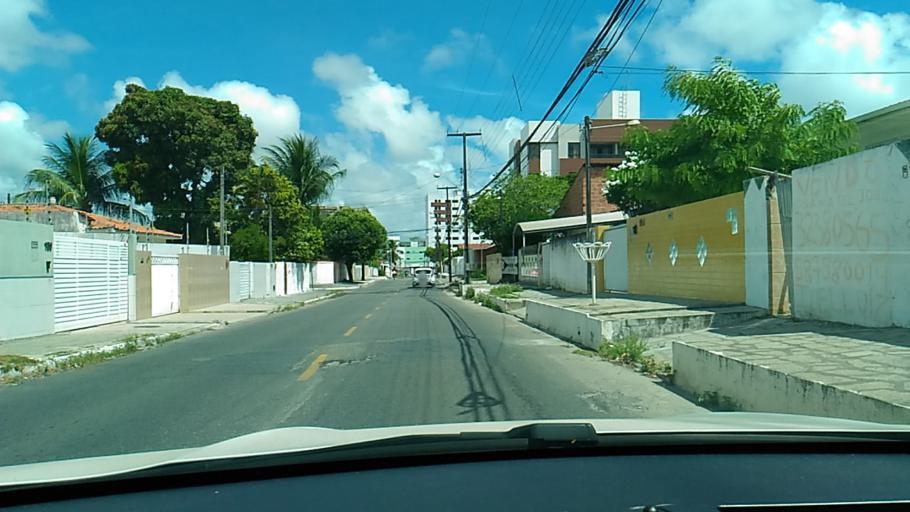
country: BR
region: Paraiba
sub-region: Joao Pessoa
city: Joao Pessoa
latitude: -7.1555
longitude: -34.8415
